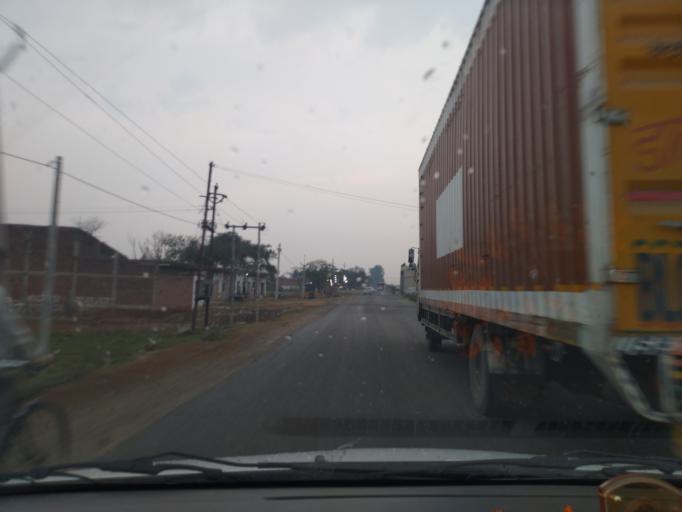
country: IN
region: Bihar
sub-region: Kaimur District
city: Bhabua
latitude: 25.1088
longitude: 83.7006
